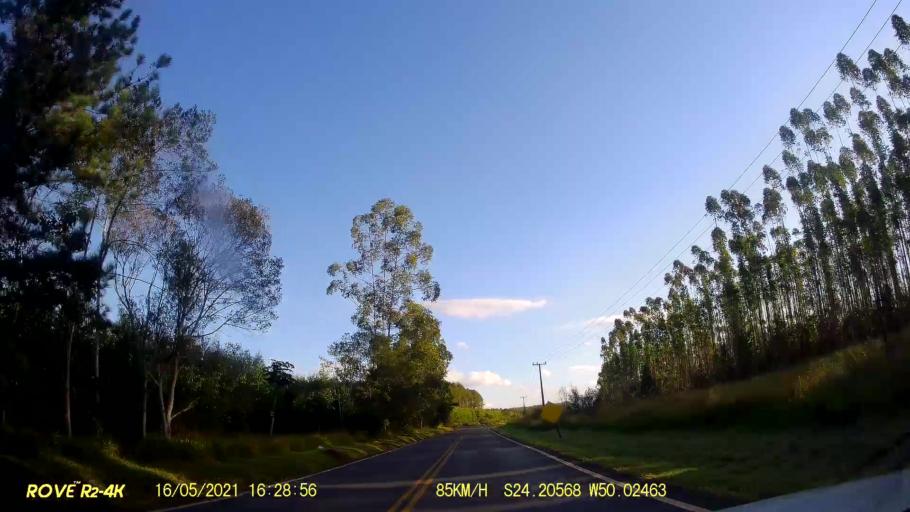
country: BR
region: Parana
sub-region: Jaguariaiva
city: Jaguariaiva
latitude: -24.2058
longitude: -50.0247
